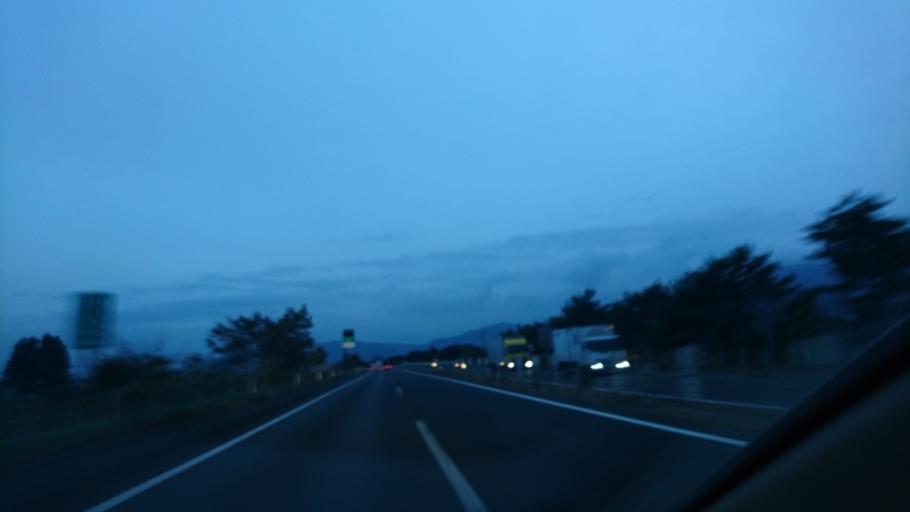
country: JP
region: Iwate
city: Morioka-shi
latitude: 39.6055
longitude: 141.1247
